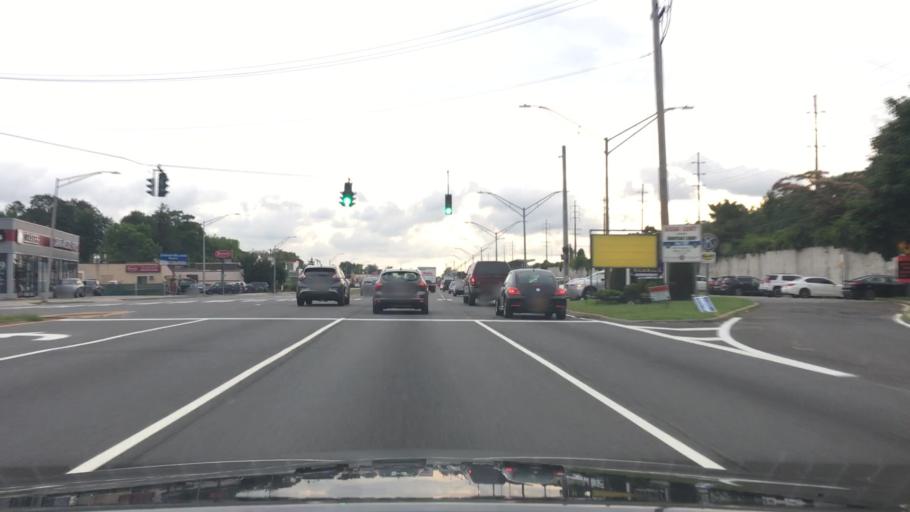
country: US
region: New York
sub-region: Nassau County
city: Merrick
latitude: 40.6649
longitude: -73.5444
